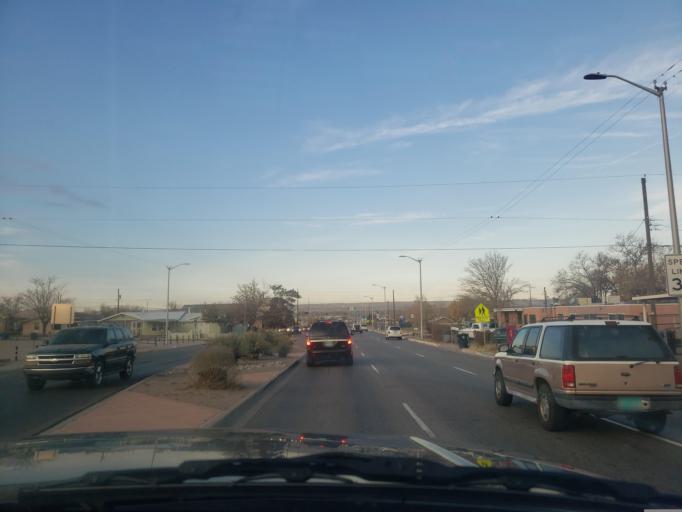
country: US
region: New Mexico
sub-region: Bernalillo County
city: Albuquerque
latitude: 35.0698
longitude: -106.6409
